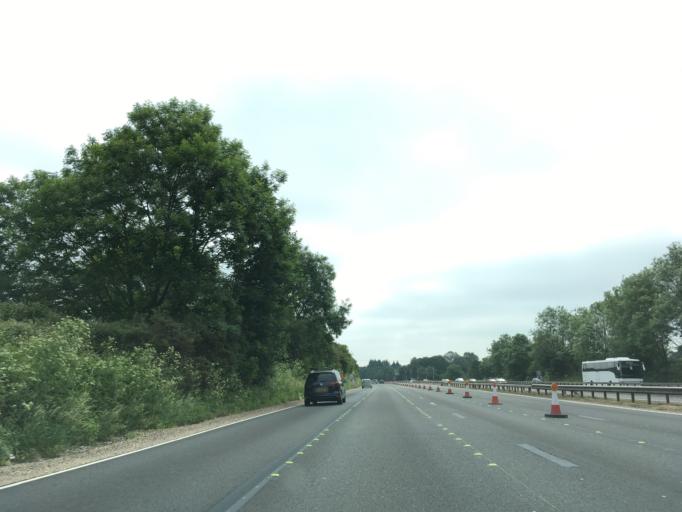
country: GB
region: England
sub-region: West Berkshire
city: Hermitage
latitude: 51.4648
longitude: -1.2612
